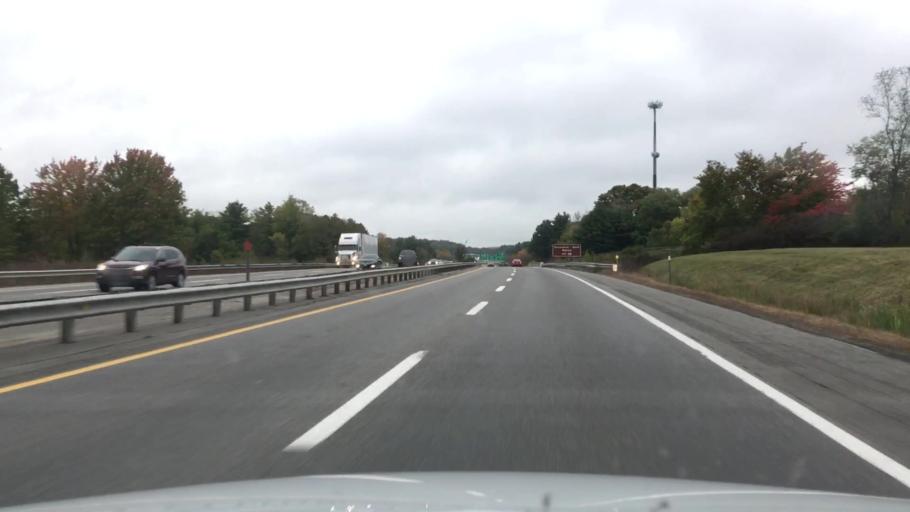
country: US
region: Maine
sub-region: Cumberland County
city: Falmouth
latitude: 43.7142
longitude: -70.3066
